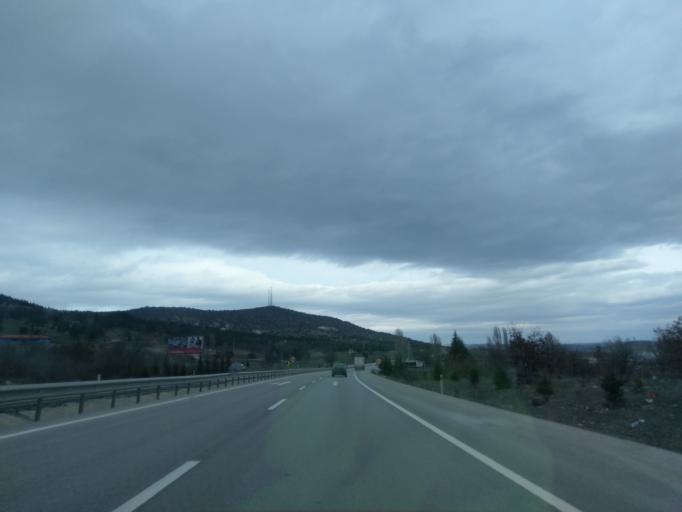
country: TR
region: Kuetahya
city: Sabuncu
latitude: 39.6027
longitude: 30.1463
